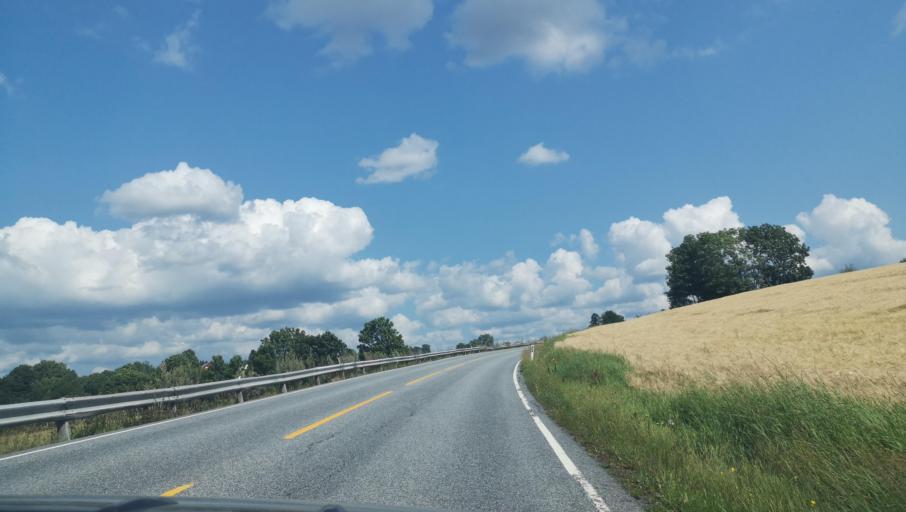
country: NO
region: Buskerud
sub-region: Ovre Eiker
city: Hokksund
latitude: 59.7284
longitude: 9.8377
